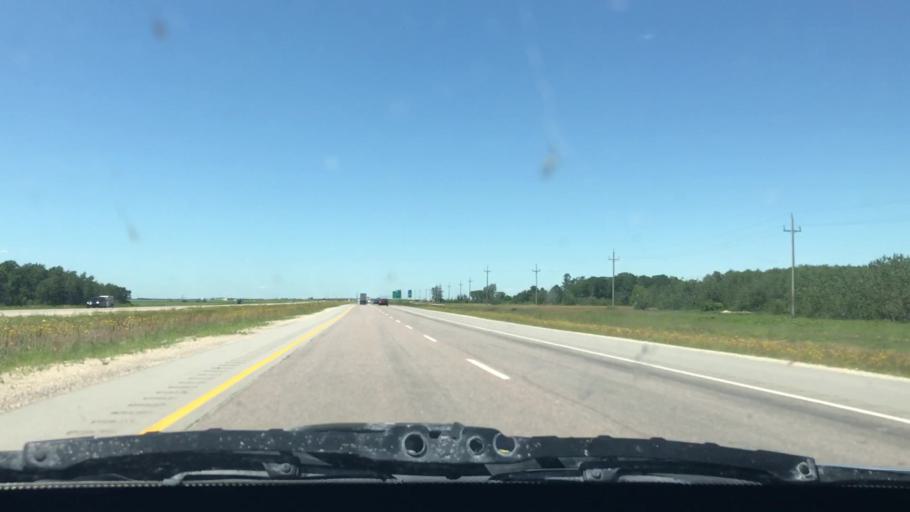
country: CA
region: Manitoba
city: Steinbach
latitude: 49.6864
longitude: -96.6090
